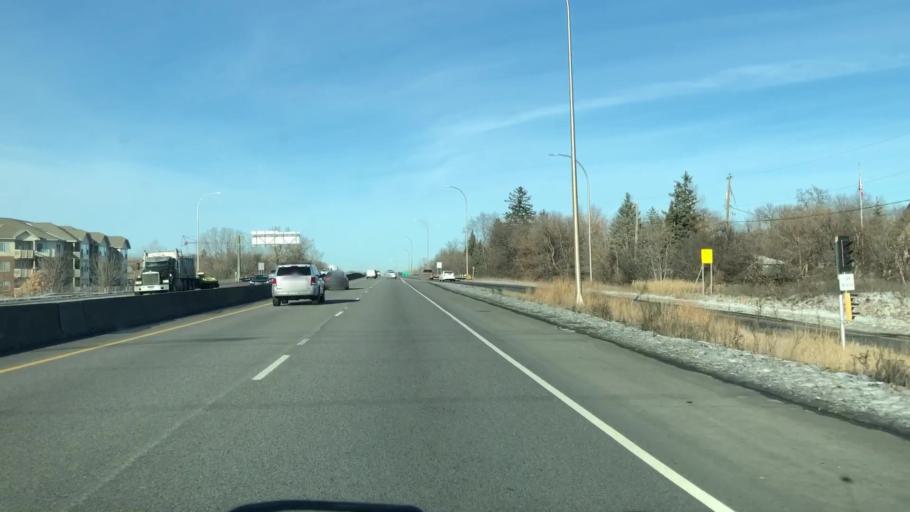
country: US
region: Minnesota
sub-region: Hennepin County
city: Minnetonka Mills
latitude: 44.9478
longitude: -93.3999
